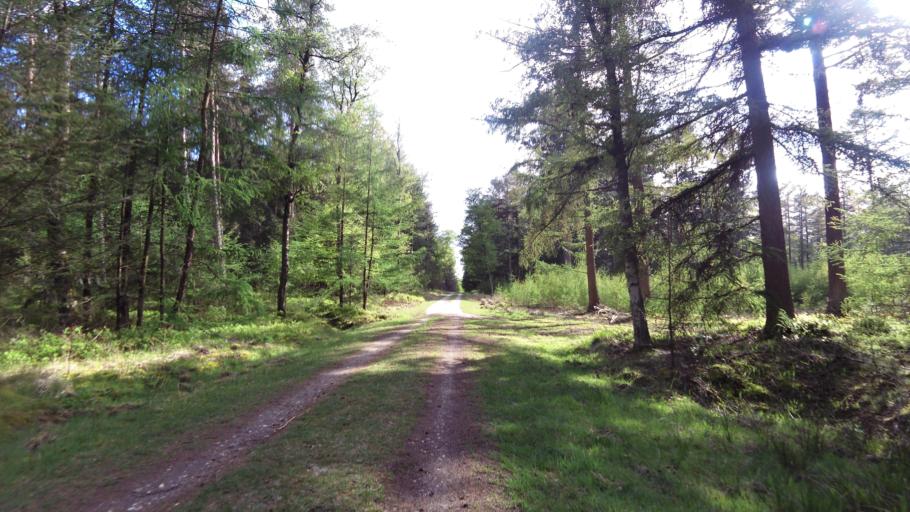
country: NL
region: Gelderland
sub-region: Gemeente Apeldoorn
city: Loenen
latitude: 52.0856
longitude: 5.9627
